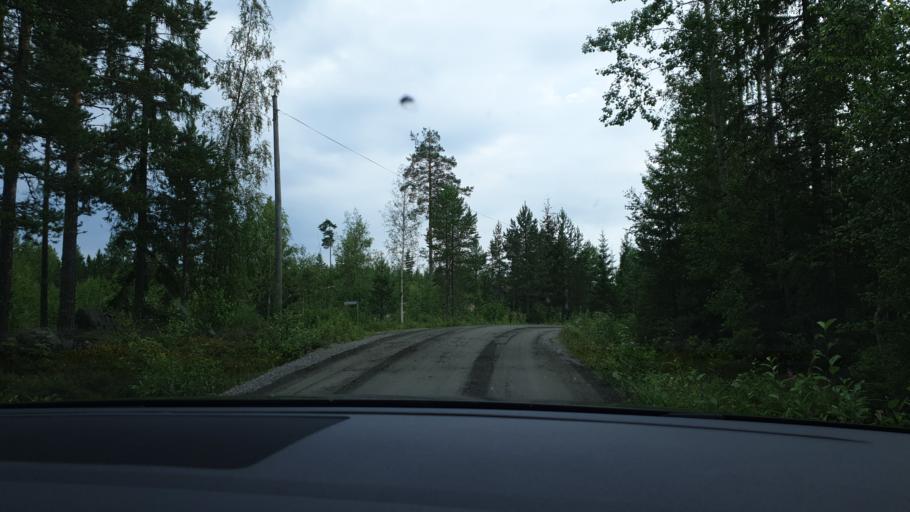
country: SE
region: Gaevleborg
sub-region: Hudiksvalls Kommun
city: Iggesund
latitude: 61.5158
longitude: 17.0177
